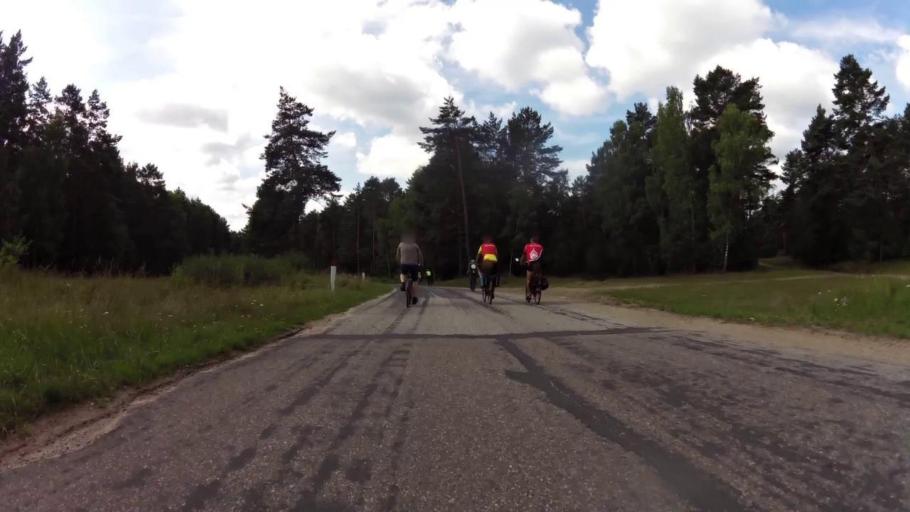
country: PL
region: West Pomeranian Voivodeship
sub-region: Powiat drawski
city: Drawsko Pomorskie
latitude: 53.4652
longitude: 15.7777
